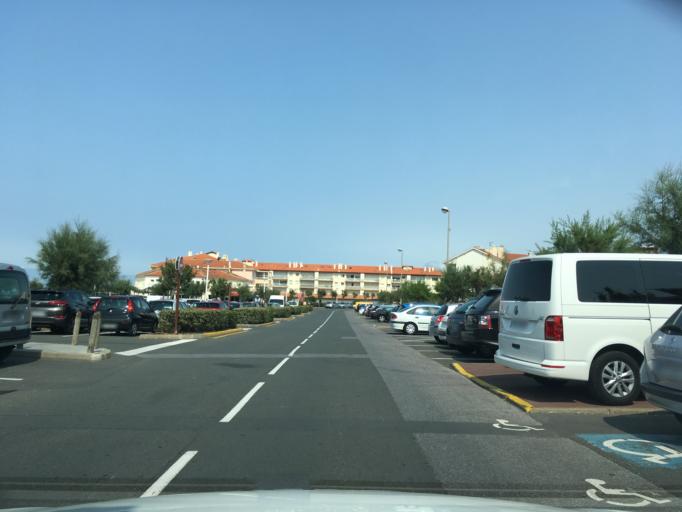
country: FR
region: Aquitaine
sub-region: Departement des Pyrenees-Atlantiques
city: Biarritz
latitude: 43.4992
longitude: -1.5424
